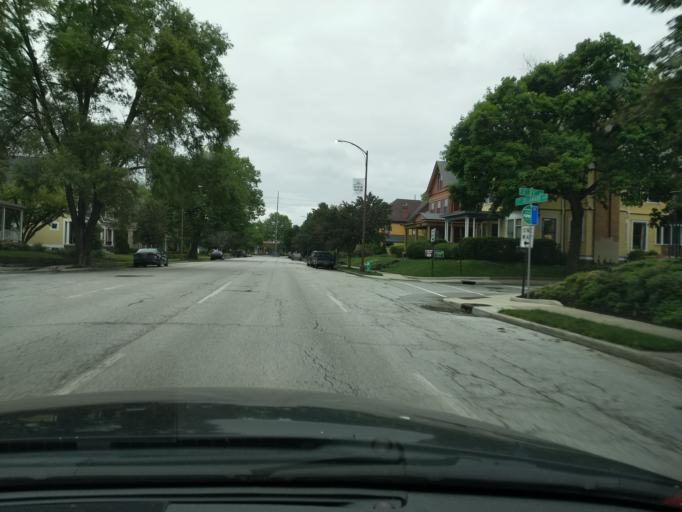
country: US
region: Indiana
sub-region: Marion County
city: Indianapolis
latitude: 39.7956
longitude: -86.1538
